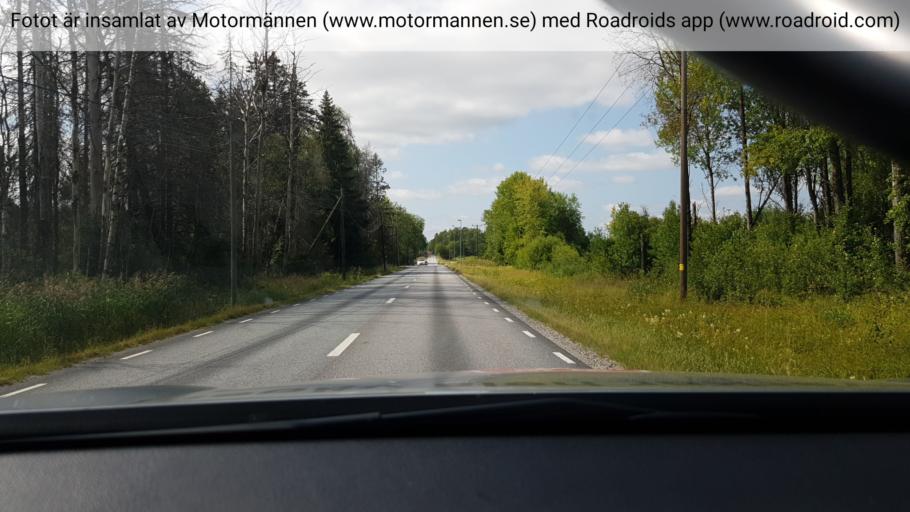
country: SE
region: Stockholm
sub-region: Osterakers Kommun
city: Akersberga
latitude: 59.5523
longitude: 18.2139
